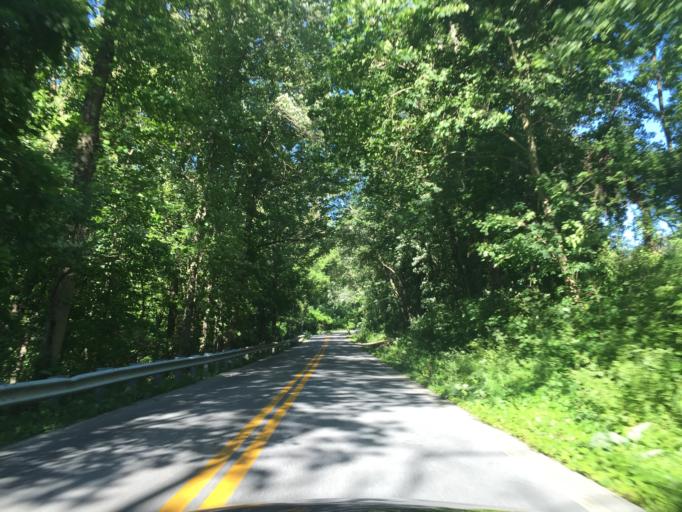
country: US
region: Maryland
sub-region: Carroll County
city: Hampstead
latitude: 39.5579
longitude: -76.8877
